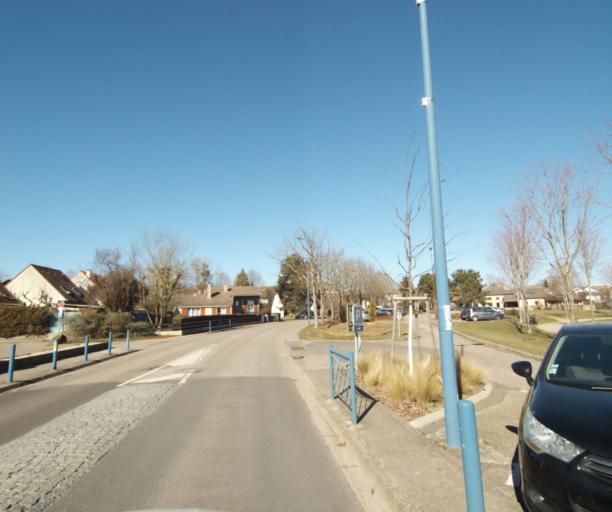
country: FR
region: Lorraine
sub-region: Departement de Meurthe-et-Moselle
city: Vandoeuvre-les-Nancy
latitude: 48.6494
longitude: 6.1943
